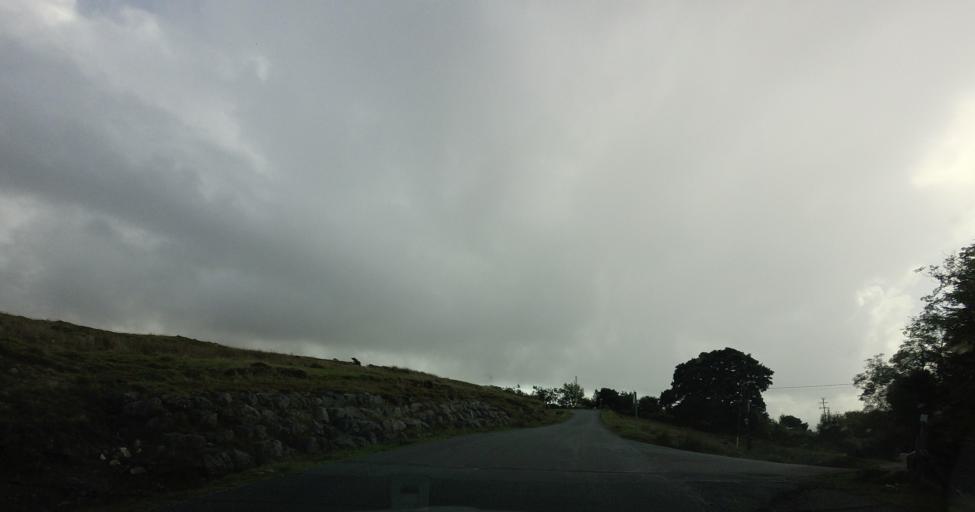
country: GB
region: Scotland
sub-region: Highland
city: Portree
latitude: 57.2122
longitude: -6.0082
